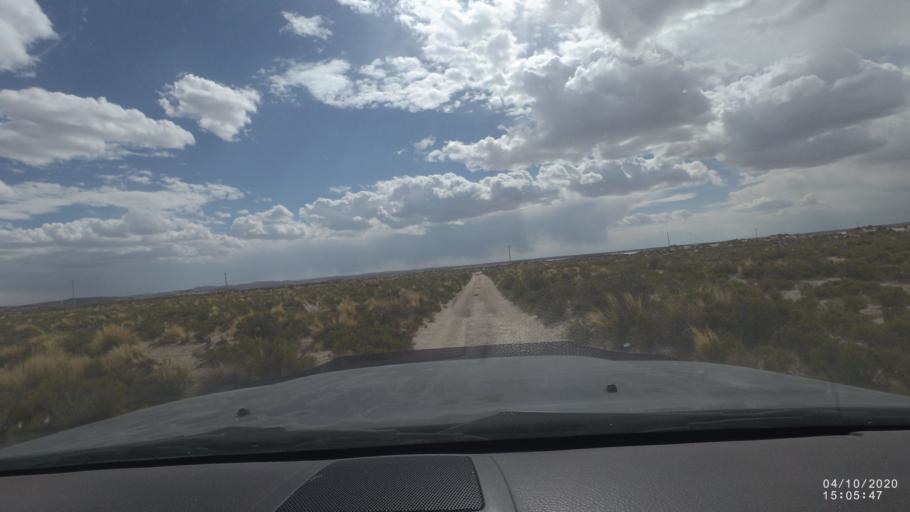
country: BO
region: Oruro
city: Poopo
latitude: -18.6936
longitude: -67.5555
